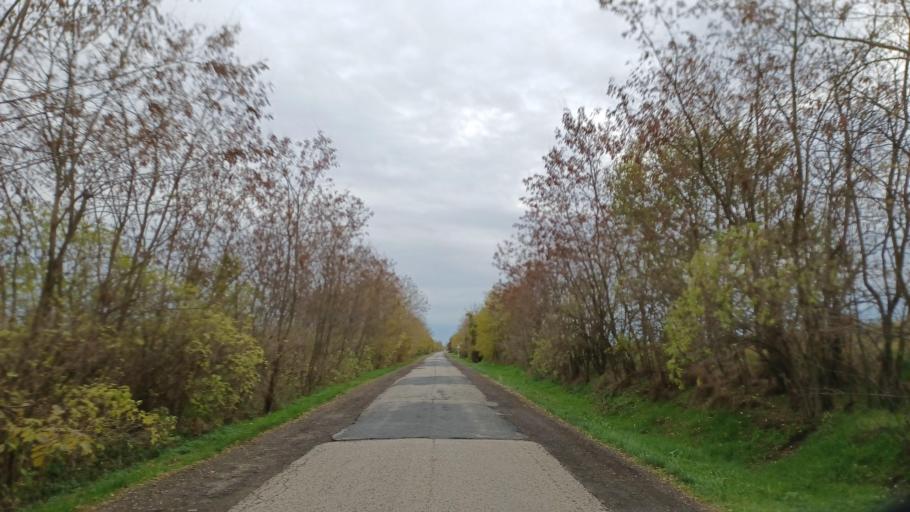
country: HU
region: Tolna
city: Simontornya
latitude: 46.6925
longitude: 18.5923
